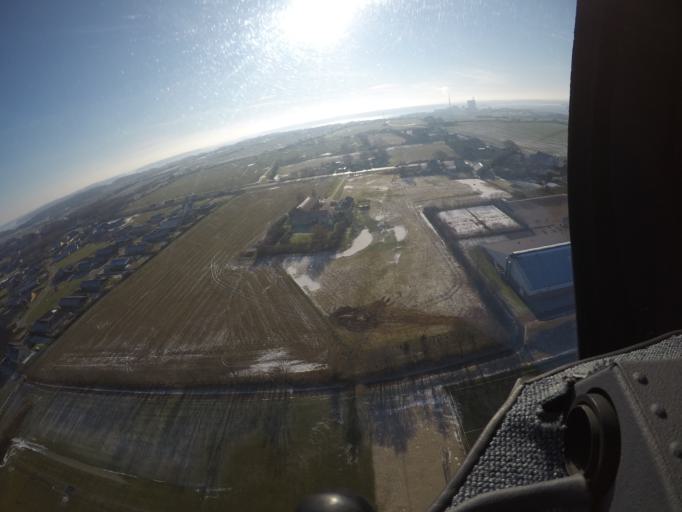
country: DK
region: South Denmark
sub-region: Fredericia Kommune
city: Taulov
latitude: 55.5348
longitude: 9.6235
